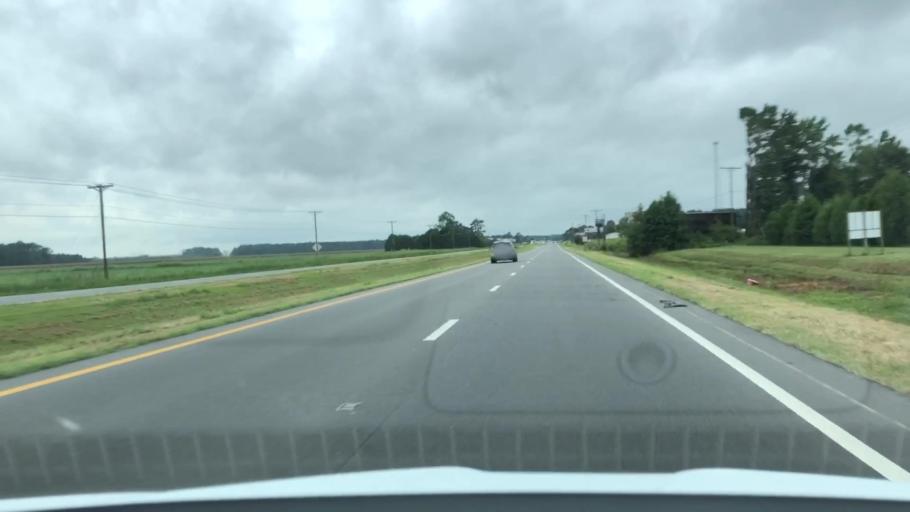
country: US
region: North Carolina
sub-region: Lenoir County
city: La Grange
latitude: 35.2608
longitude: -77.7144
